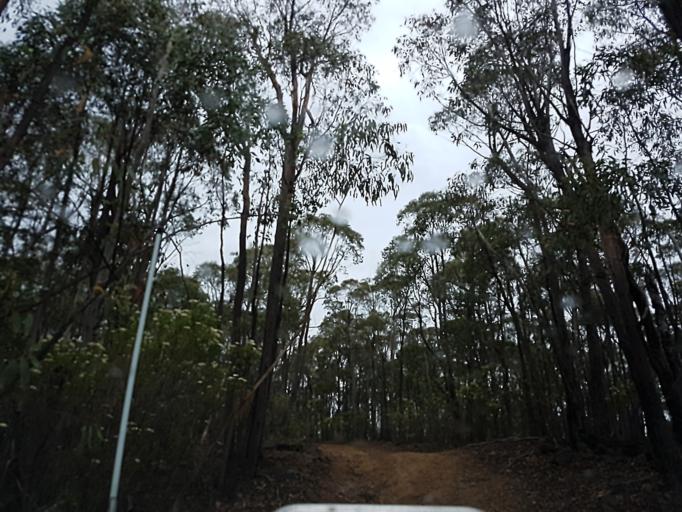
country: AU
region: New South Wales
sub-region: Snowy River
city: Jindabyne
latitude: -36.8736
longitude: 148.3319
